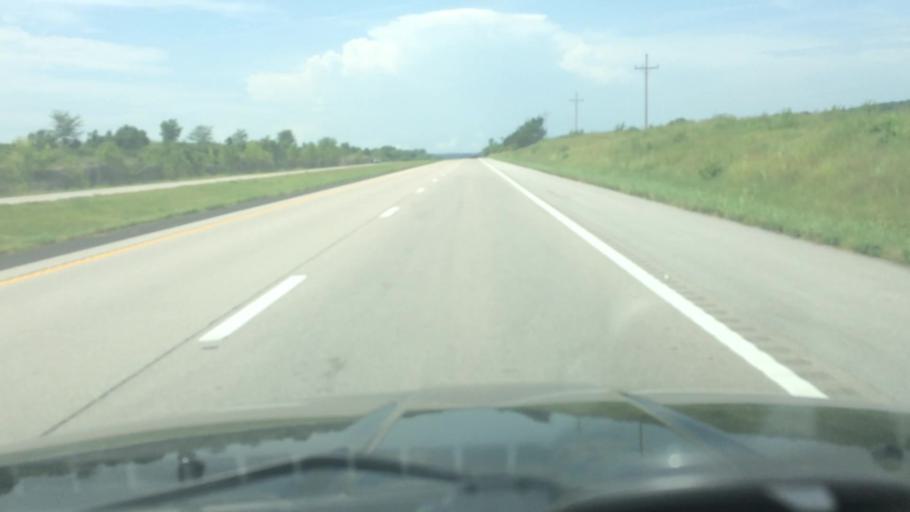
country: US
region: Missouri
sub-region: Polk County
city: Humansville
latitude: 37.8000
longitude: -93.5941
